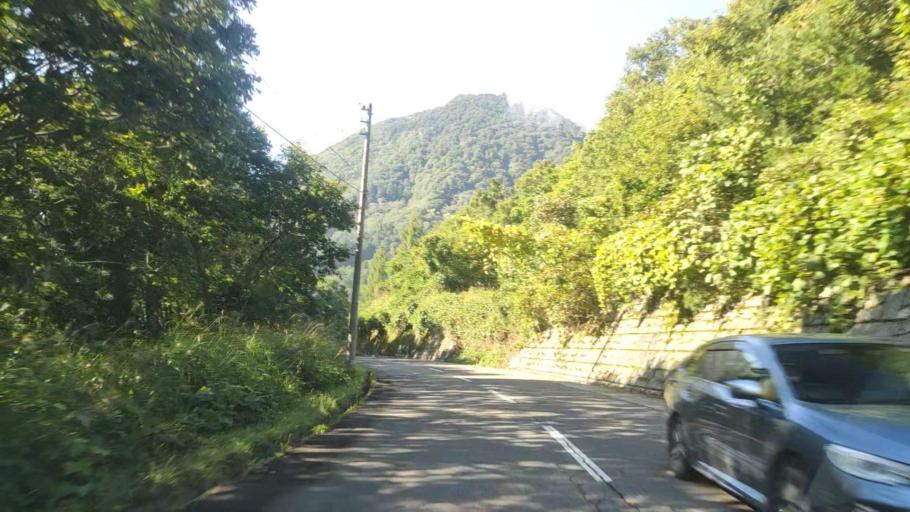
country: JP
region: Nagano
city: Iiyama
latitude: 36.8149
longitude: 138.4141
